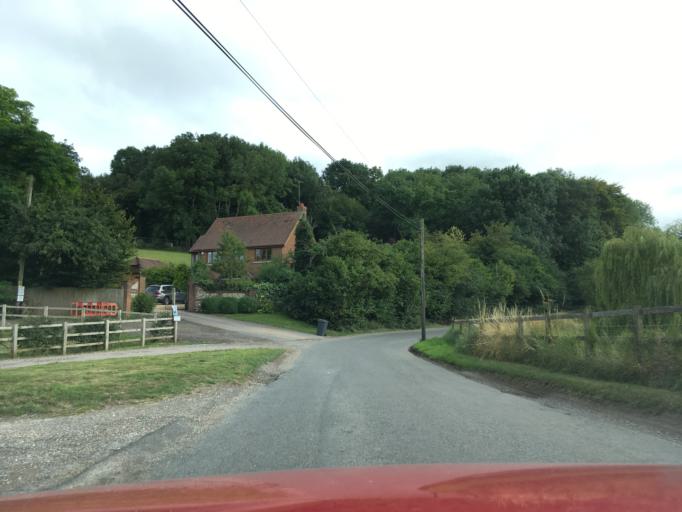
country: GB
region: England
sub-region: Hampshire
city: Colden Common
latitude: 50.9999
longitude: -1.2724
